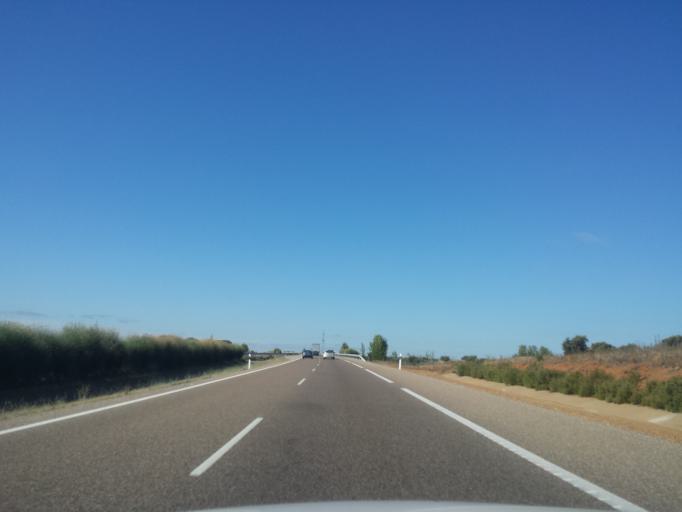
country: ES
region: Castille and Leon
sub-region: Provincia de Leon
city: Villamandos
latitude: 42.1812
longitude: -5.6280
